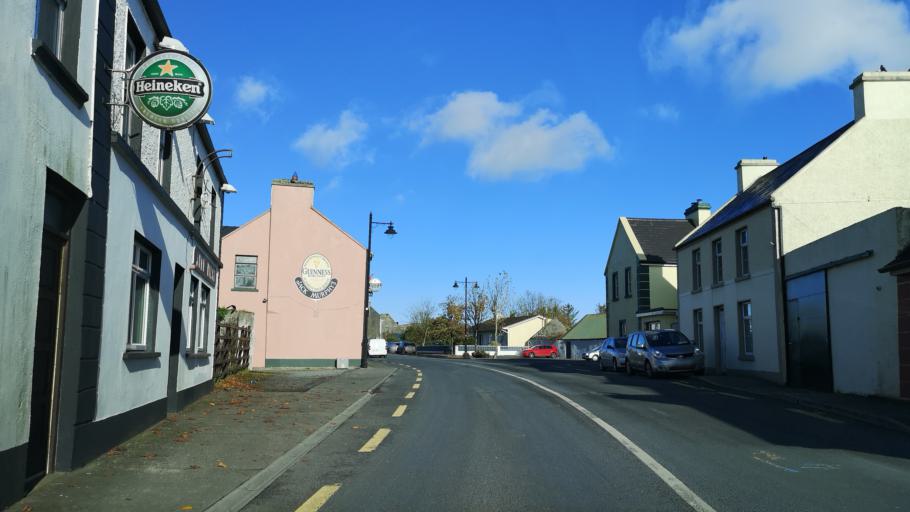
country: IE
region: Connaught
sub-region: Maigh Eo
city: Ballinrobe
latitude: 53.5795
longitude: -9.1220
